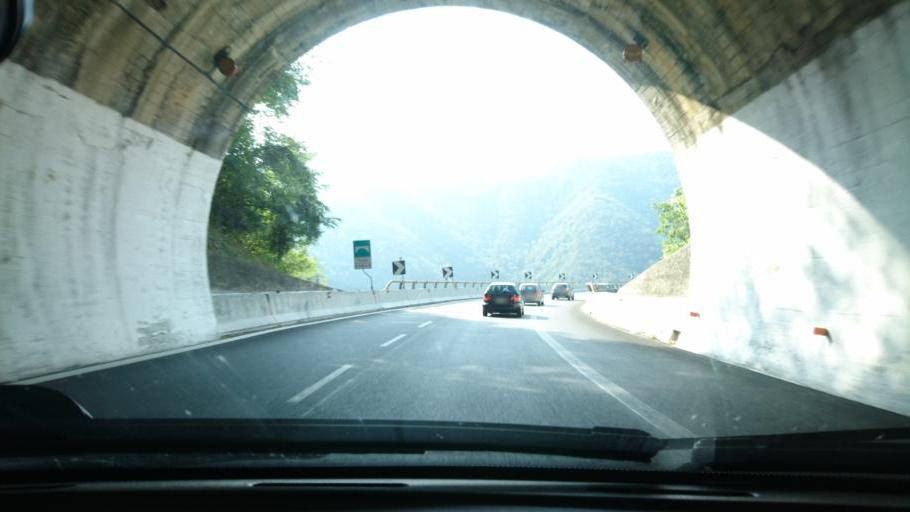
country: IT
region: Liguria
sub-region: Provincia di Savona
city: Quiliano
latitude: 44.3164
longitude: 8.3793
